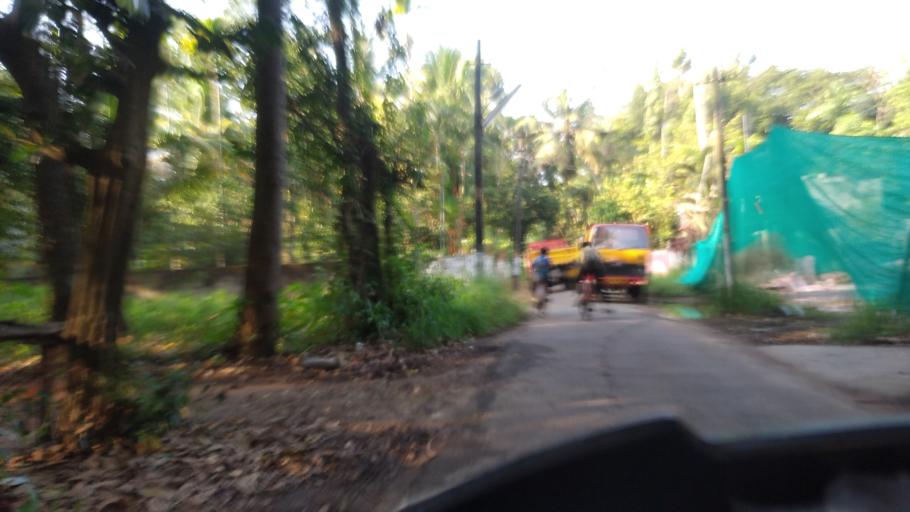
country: IN
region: Kerala
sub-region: Ernakulam
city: Elur
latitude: 10.0415
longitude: 76.2277
